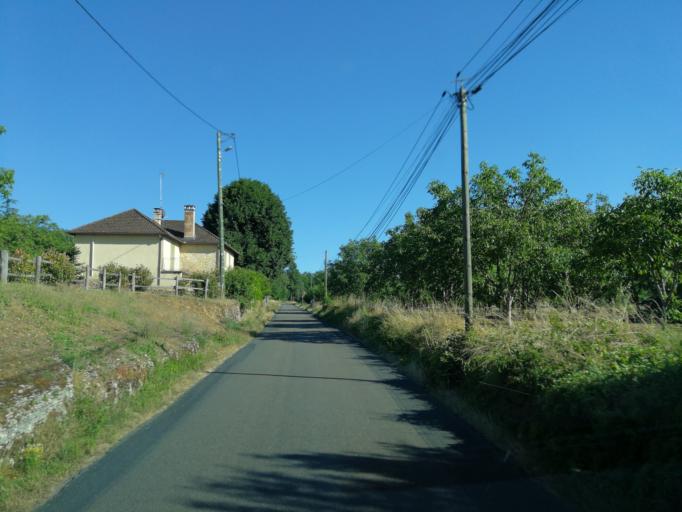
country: FR
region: Midi-Pyrenees
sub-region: Departement du Lot
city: Gourdon
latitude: 44.7765
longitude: 1.3657
